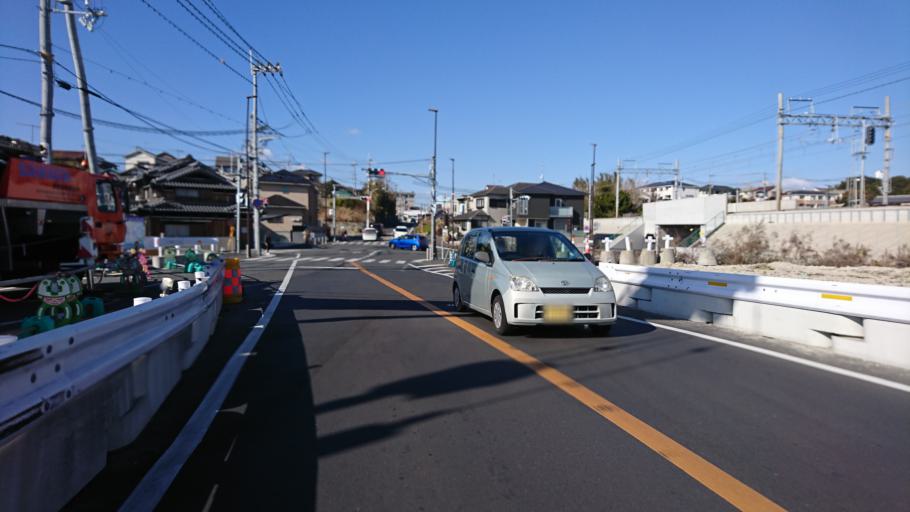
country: JP
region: Hyogo
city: Akashi
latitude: 34.6667
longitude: 134.9419
